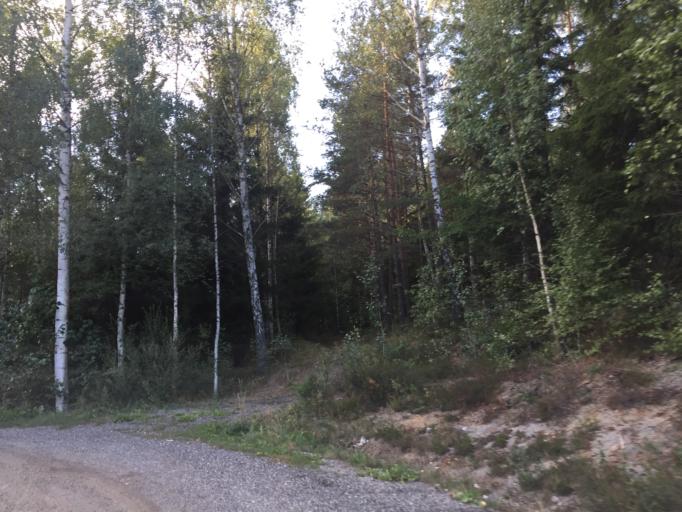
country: NO
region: Ostfold
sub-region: Trogstad
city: Skjonhaug
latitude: 59.6451
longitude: 11.3382
